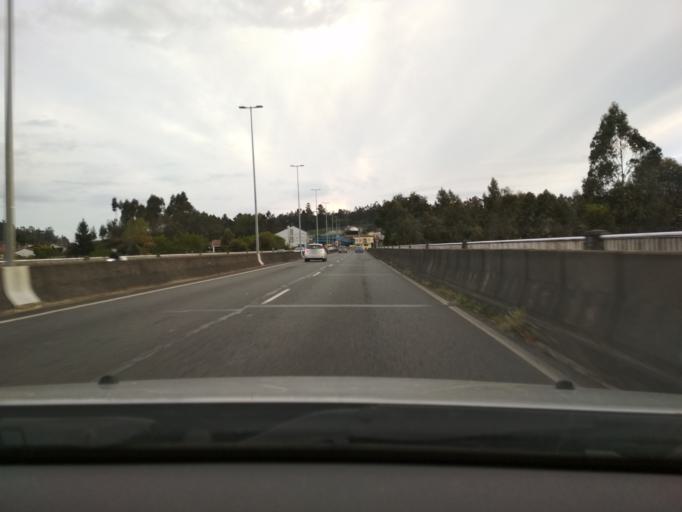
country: ES
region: Galicia
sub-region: Provincia da Coruna
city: Santiago de Compostela
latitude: 42.8616
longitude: -8.5699
